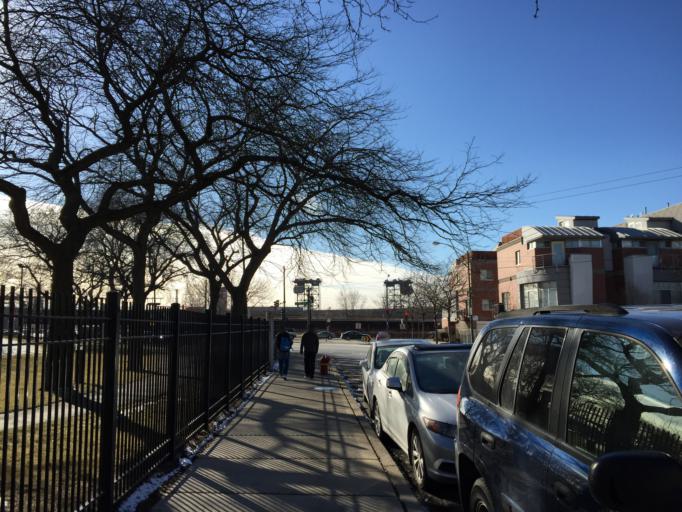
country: US
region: Illinois
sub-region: Cook County
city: Chicago
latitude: 41.8554
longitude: -87.6290
